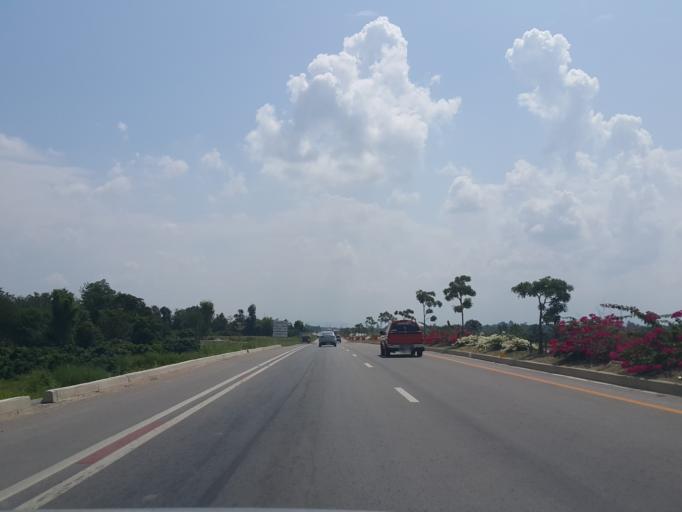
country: TH
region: Chiang Mai
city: Mae Wang
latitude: 18.5944
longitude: 98.8349
